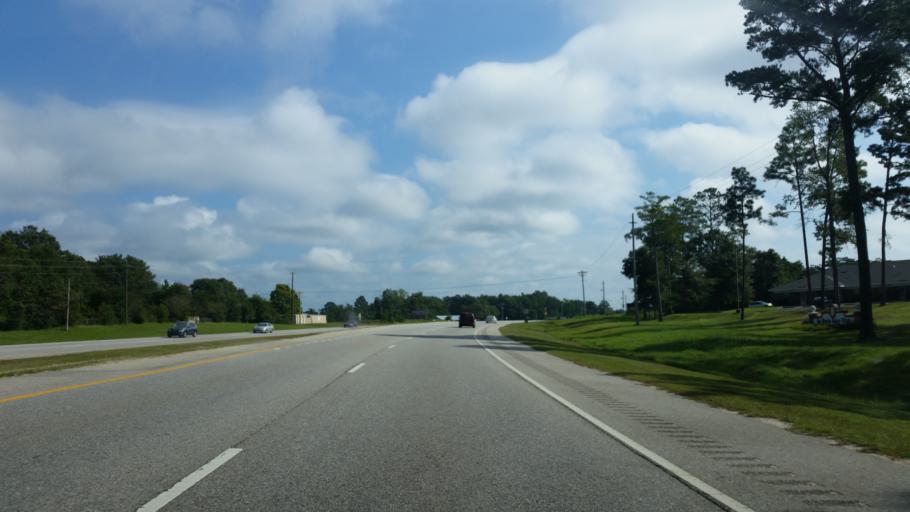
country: US
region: Alabama
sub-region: Baldwin County
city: Bay Minette
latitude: 30.9075
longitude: -87.7912
